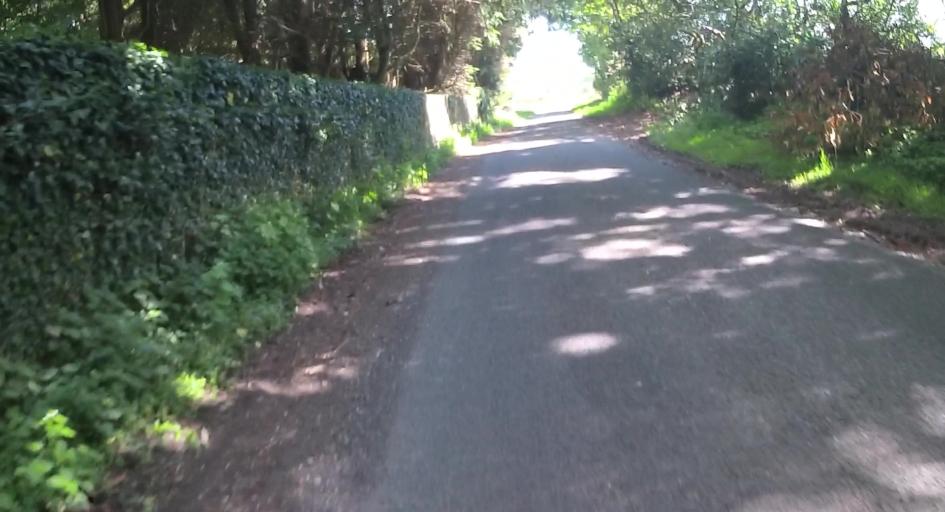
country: GB
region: England
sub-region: Hampshire
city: Four Marks
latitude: 51.1464
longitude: -1.0234
